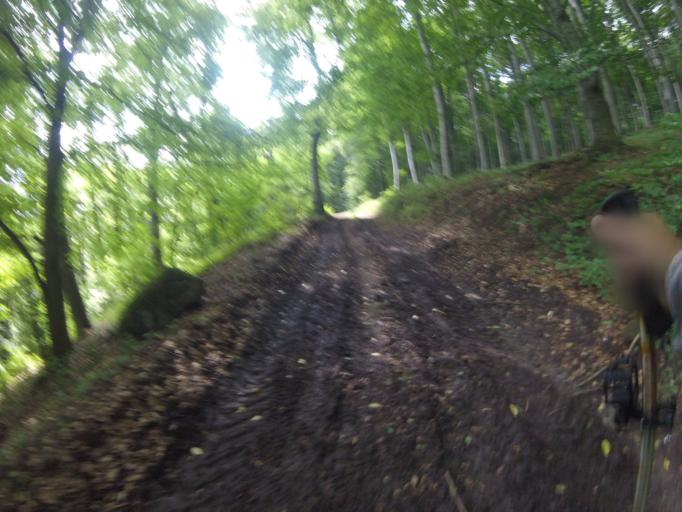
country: SK
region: Nitriansky
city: Sahy
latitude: 47.9610
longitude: 18.8809
